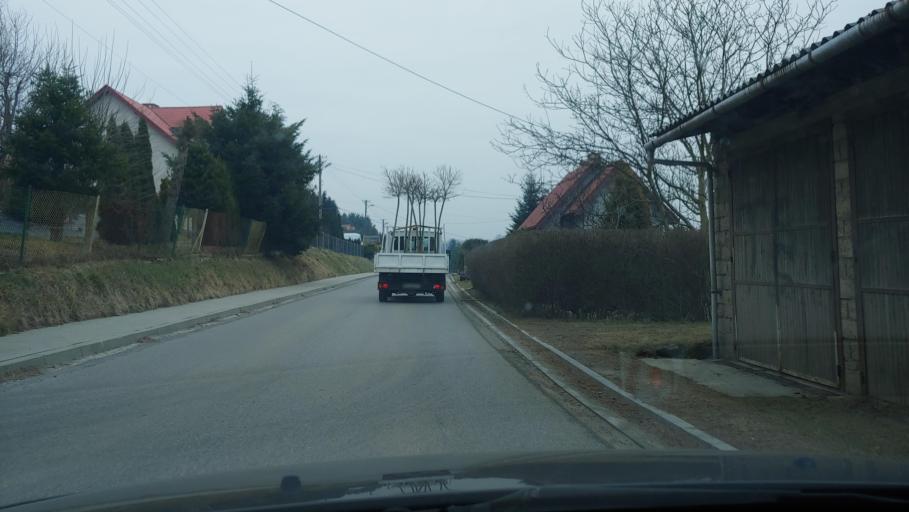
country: PL
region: Lesser Poland Voivodeship
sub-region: Powiat krakowski
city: Balice
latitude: 50.0929
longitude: 19.7759
